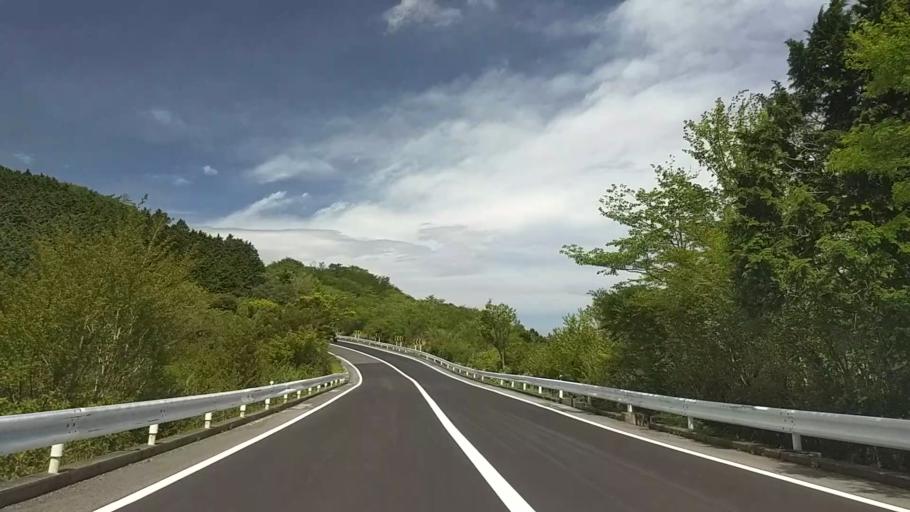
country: JP
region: Kanagawa
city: Hakone
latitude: 35.1927
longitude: 139.0641
